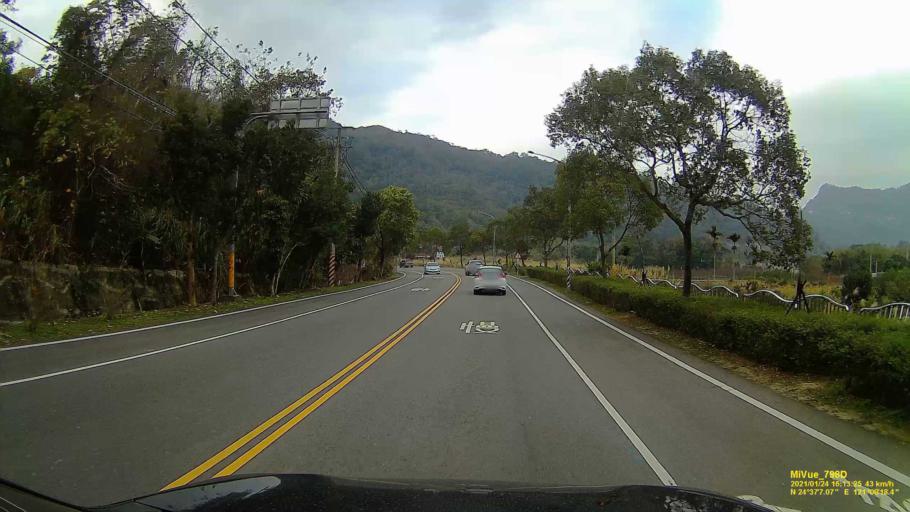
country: TW
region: Taiwan
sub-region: Hsinchu
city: Hsinchu
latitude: 24.6189
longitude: 121.0049
